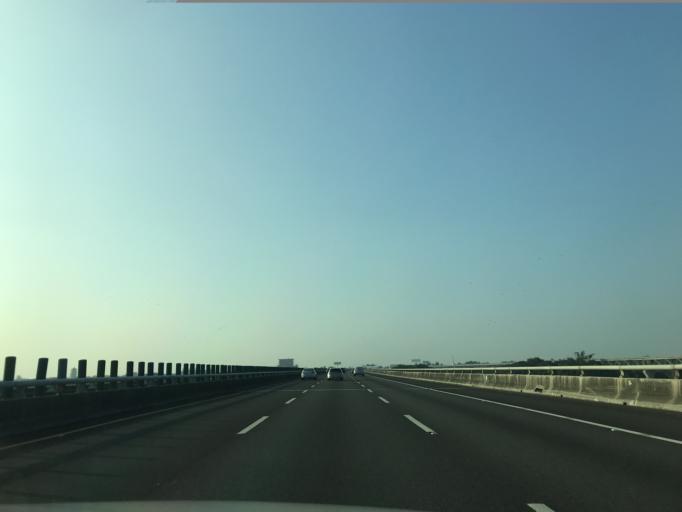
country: TW
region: Taiwan
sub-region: Yunlin
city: Douliu
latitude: 23.8057
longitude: 120.4837
